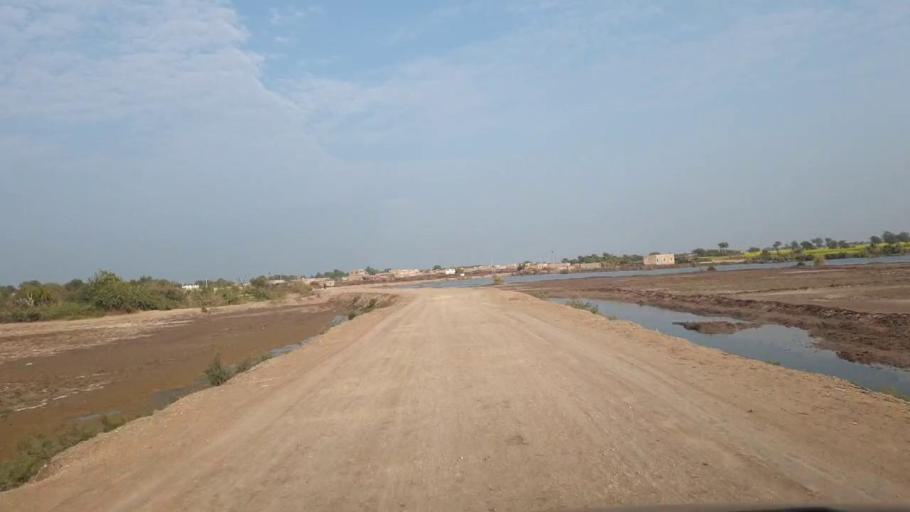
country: PK
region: Sindh
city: Shahdadpur
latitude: 25.8821
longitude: 68.7197
